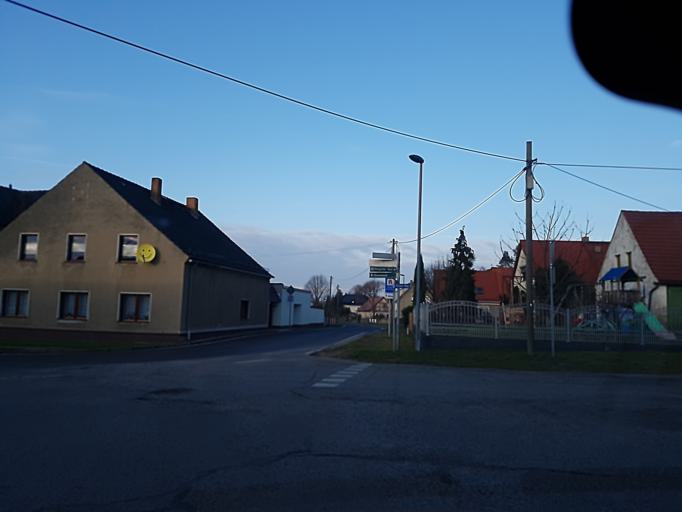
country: DE
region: Brandenburg
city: Schonborn
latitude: 51.5412
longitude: 13.4766
